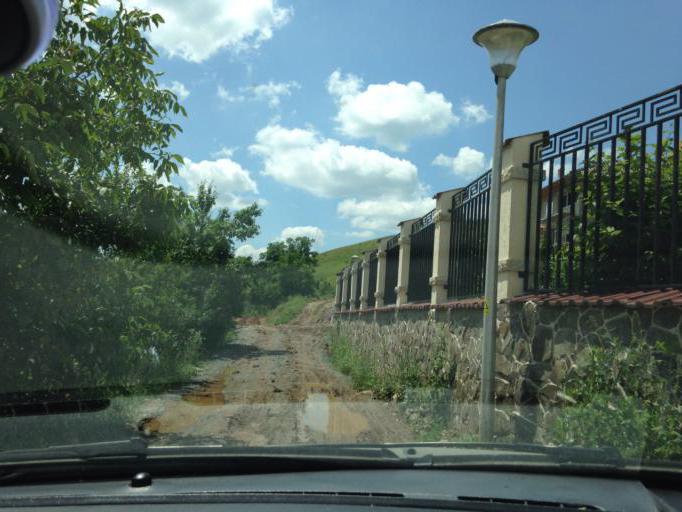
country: RO
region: Cluj
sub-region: Comuna Floresti
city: Floresti
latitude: 46.7394
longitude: 23.5317
